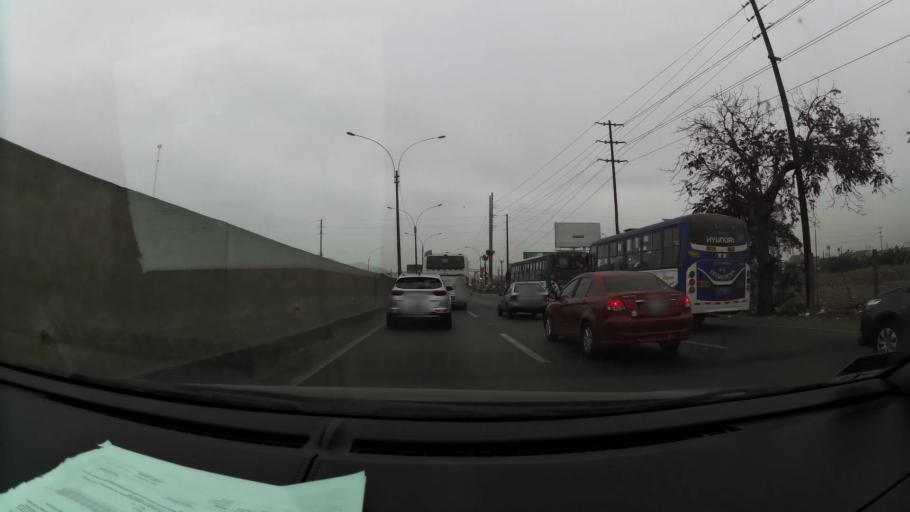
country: PE
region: Lima
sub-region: Lima
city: Independencia
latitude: -11.9317
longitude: -77.0723
